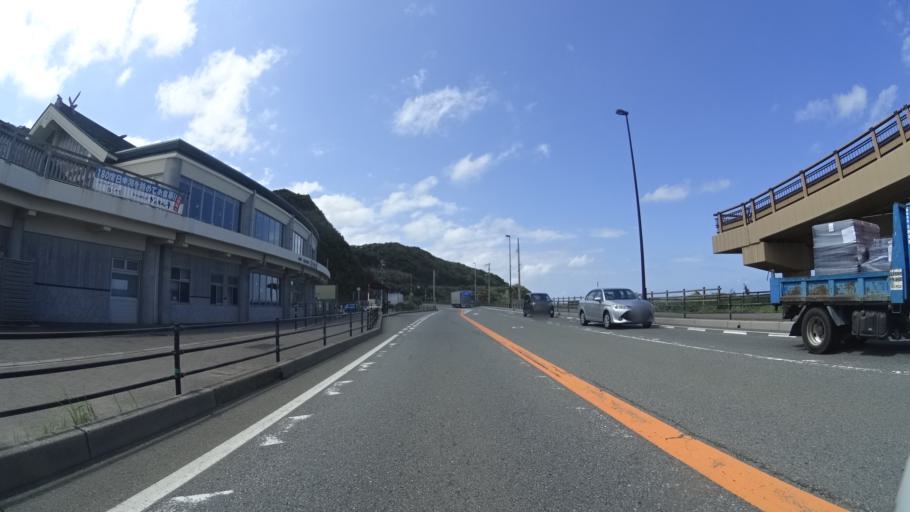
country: JP
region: Tottori
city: Tottori
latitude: 35.5257
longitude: 134.1149
